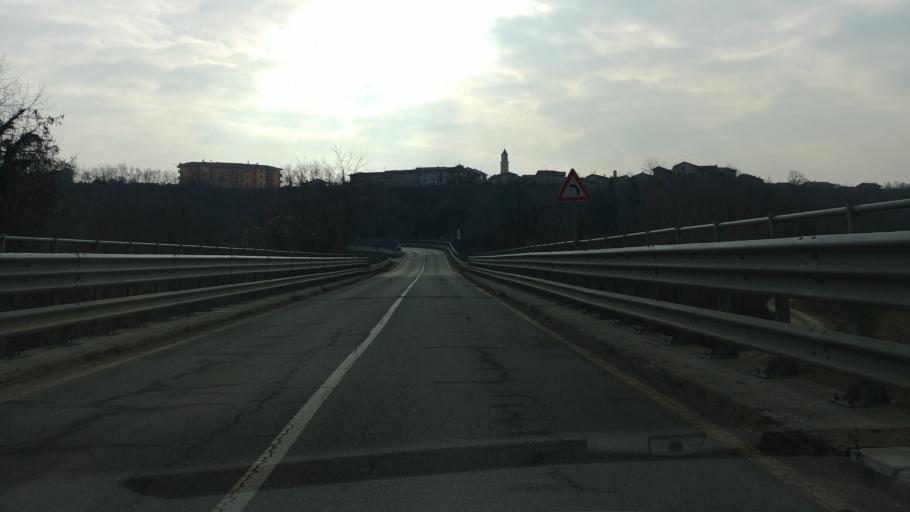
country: IT
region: Piedmont
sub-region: Provincia di Cuneo
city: Castelletto Stura
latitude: 44.4489
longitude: 7.6370
